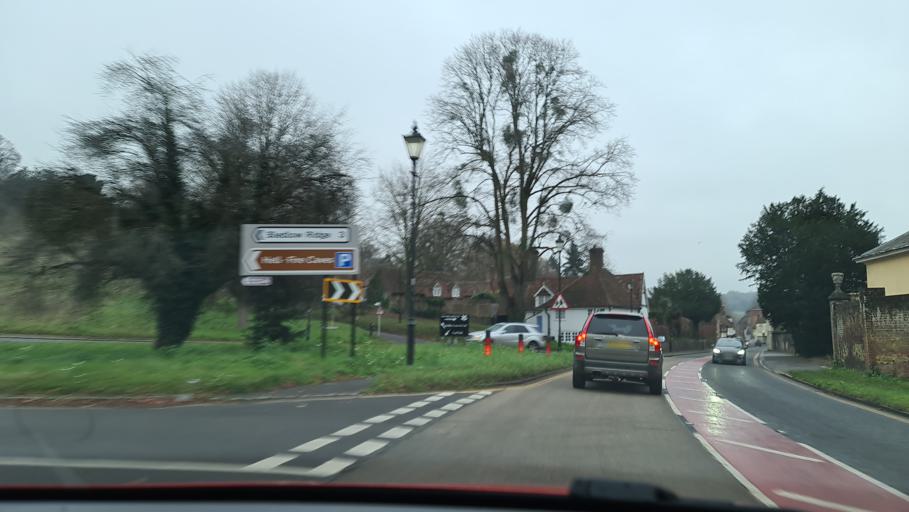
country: GB
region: England
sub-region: Buckinghamshire
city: High Wycombe
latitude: 51.6446
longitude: -0.8057
